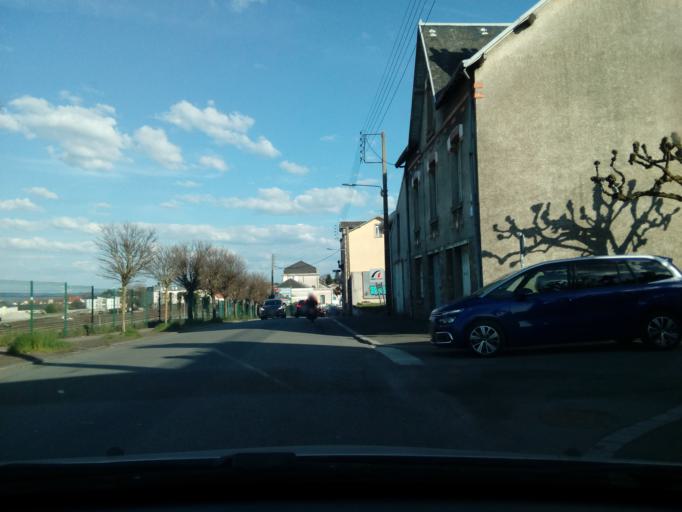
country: FR
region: Limousin
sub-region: Departement de la Creuse
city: Gueret
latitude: 46.1746
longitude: 1.8772
